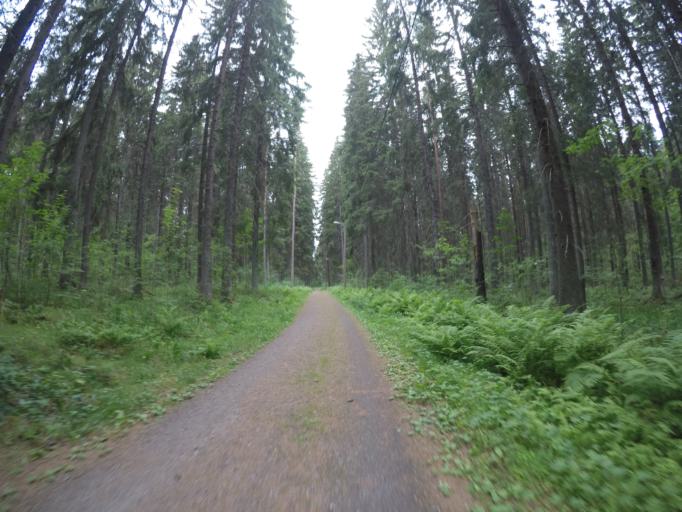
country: FI
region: Haeme
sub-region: Haemeenlinna
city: Haemeenlinna
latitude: 60.9996
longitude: 24.4078
